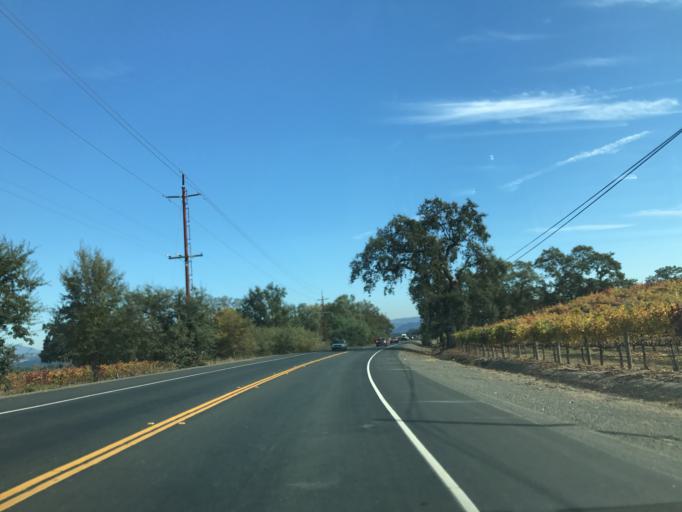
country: US
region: California
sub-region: Sonoma County
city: Windsor
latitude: 38.4892
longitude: -122.8058
